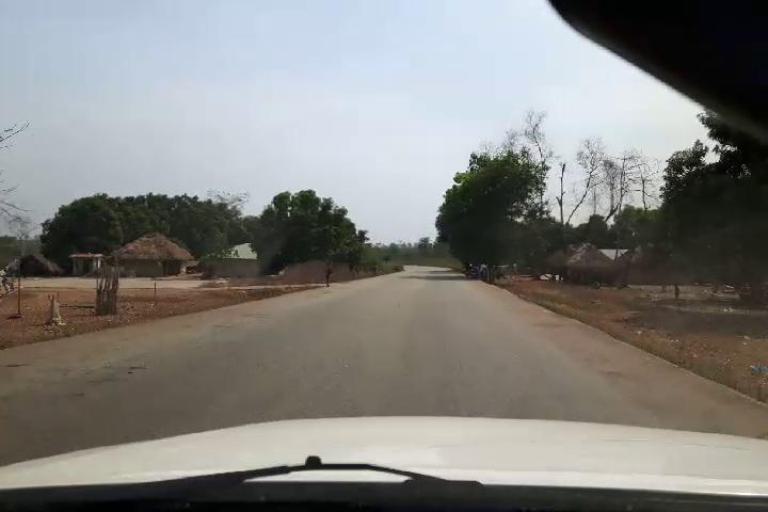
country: SL
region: Northern Province
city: Yonibana
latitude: 8.3975
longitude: -12.1944
